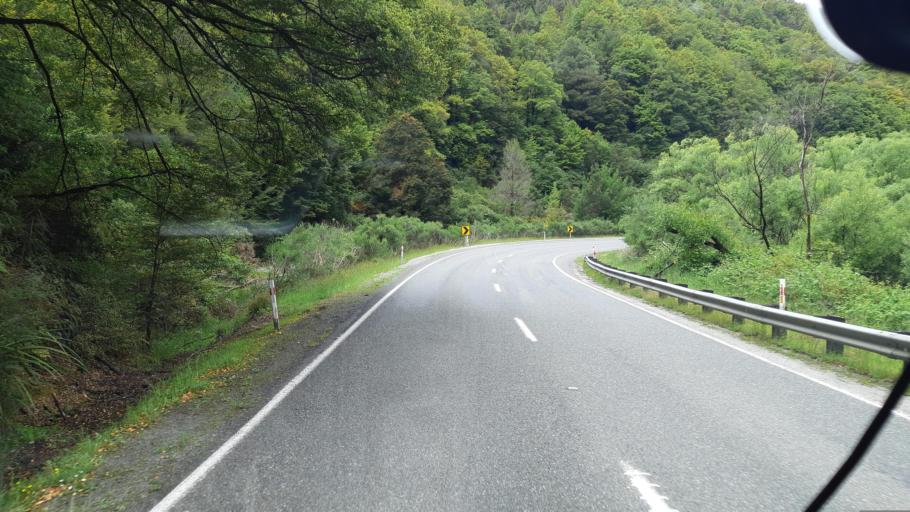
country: NZ
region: West Coast
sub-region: Buller District
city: Westport
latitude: -42.1387
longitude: 171.8905
